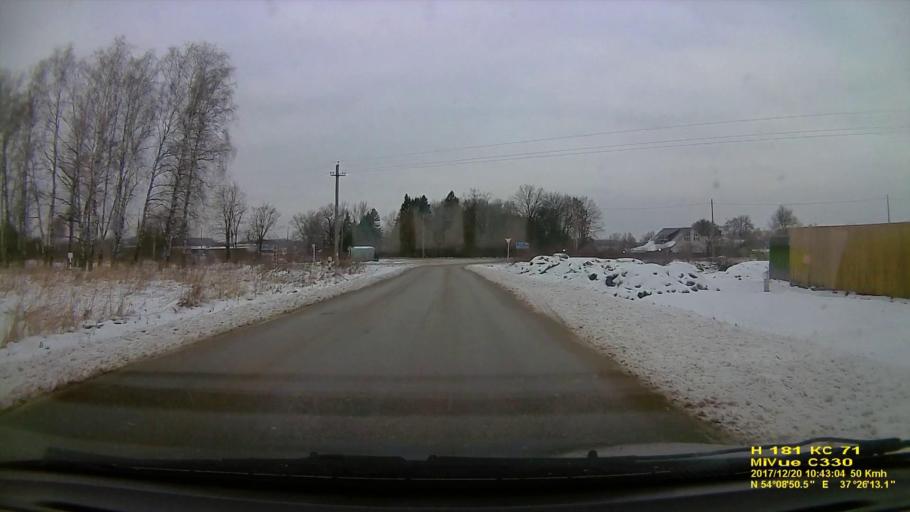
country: RU
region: Tula
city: Kosaya Gora
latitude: 54.1475
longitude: 37.4369
